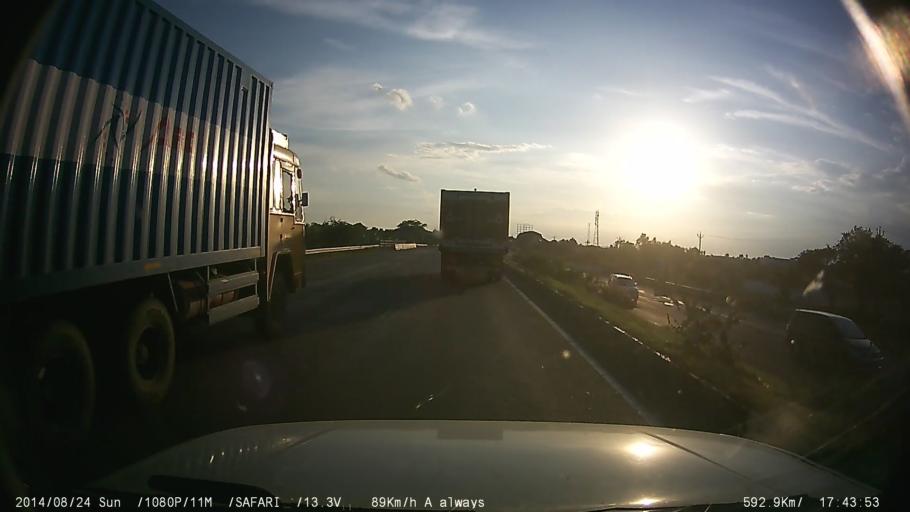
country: IN
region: Tamil Nadu
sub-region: Kancheepuram
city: Wallajahbad
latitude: 12.9046
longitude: 79.8232
